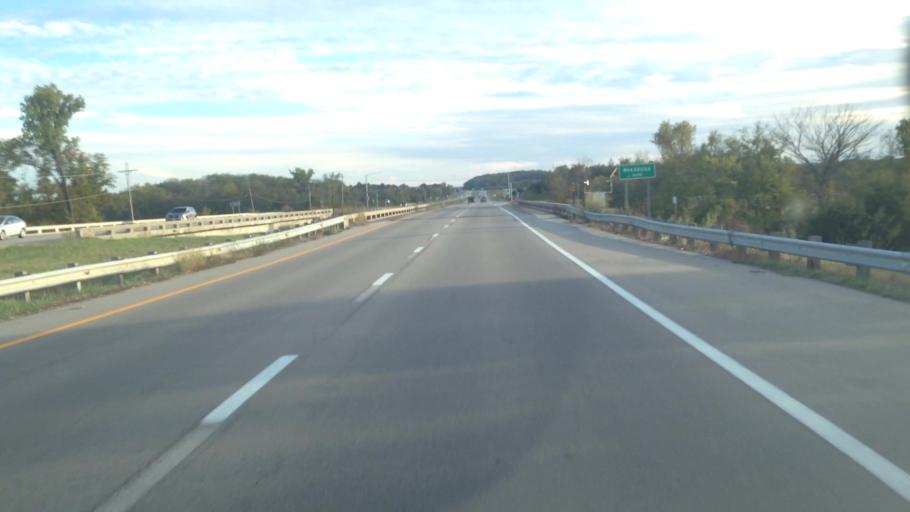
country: US
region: Kansas
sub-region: Douglas County
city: Lawrence
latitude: 38.9118
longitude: -95.2608
